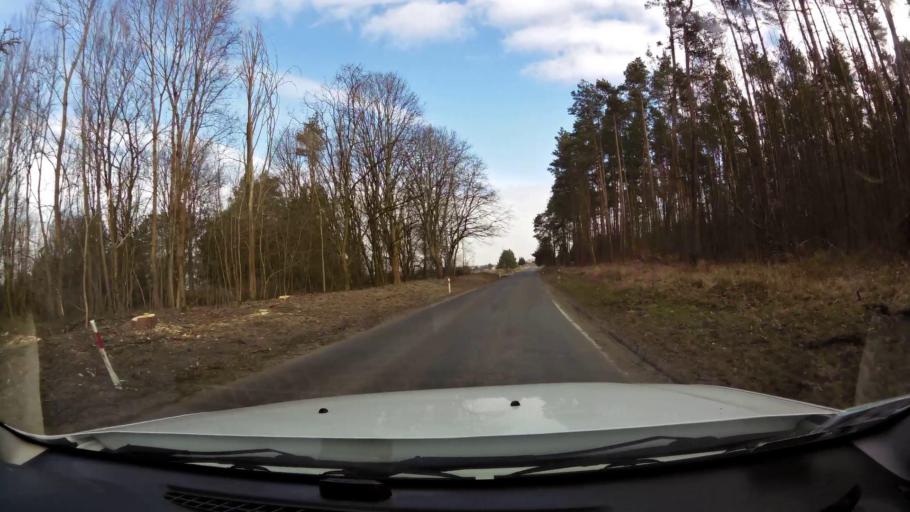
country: PL
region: West Pomeranian Voivodeship
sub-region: Powiat mysliborski
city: Debno
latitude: 52.7227
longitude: 14.6829
